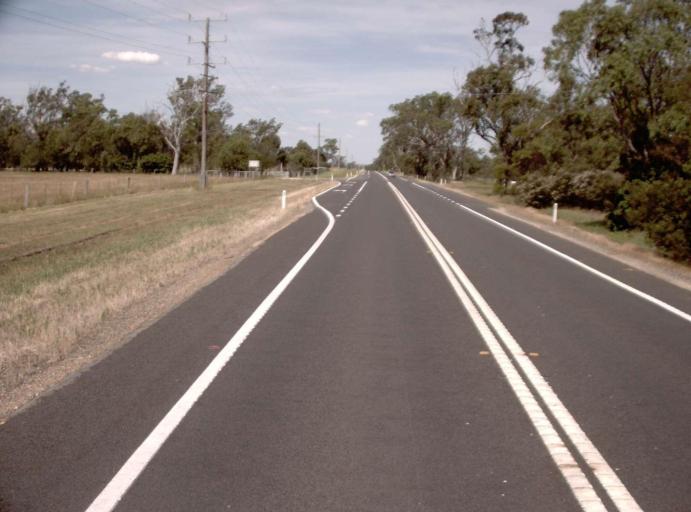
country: AU
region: Victoria
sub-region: East Gippsland
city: Bairnsdale
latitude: -37.8661
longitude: 147.4906
